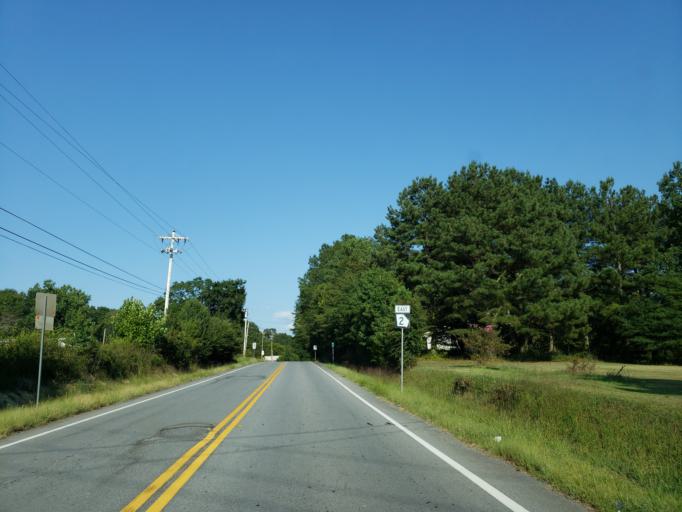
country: US
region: Tennessee
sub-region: Bradley County
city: Wildwood Lake
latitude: 34.9567
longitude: -84.7739
